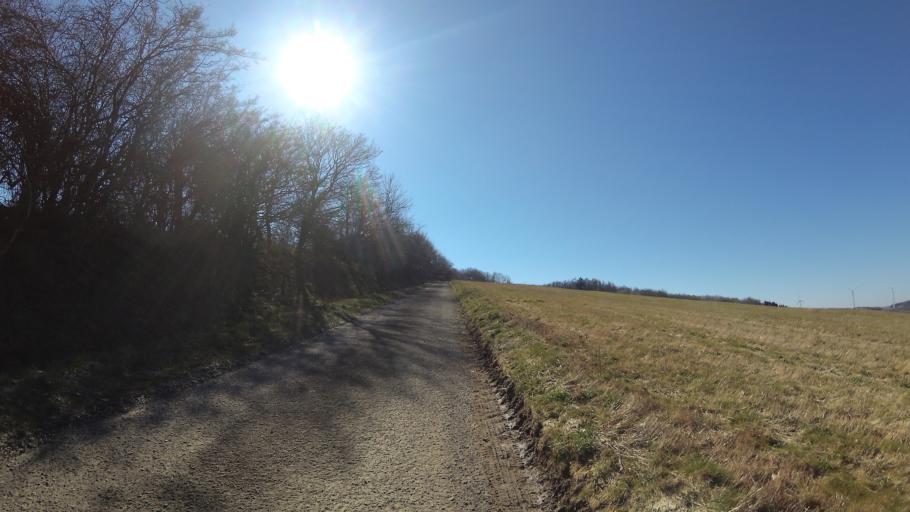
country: DE
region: Rheinland-Pfalz
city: Breitenbach
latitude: 49.4561
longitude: 7.2478
